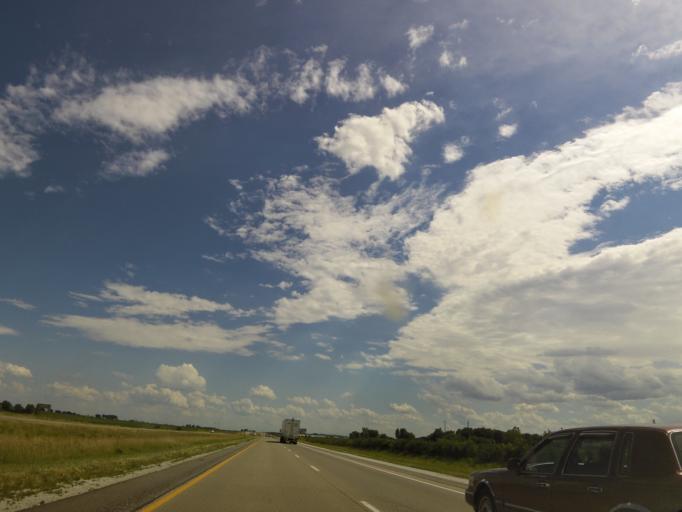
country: US
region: Iowa
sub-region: Henry County
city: Winfield
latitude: 41.1406
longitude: -91.5402
